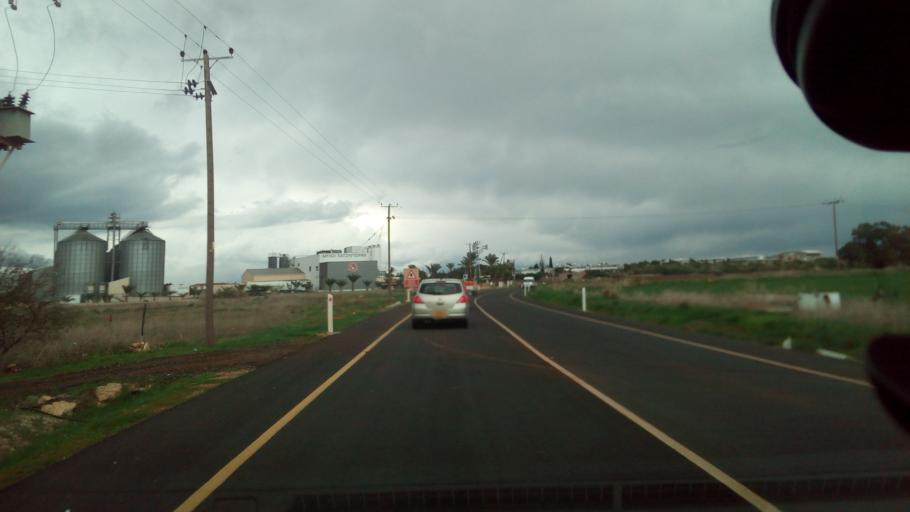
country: CY
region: Ammochostos
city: Frenaros
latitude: 35.0260
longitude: 33.9096
